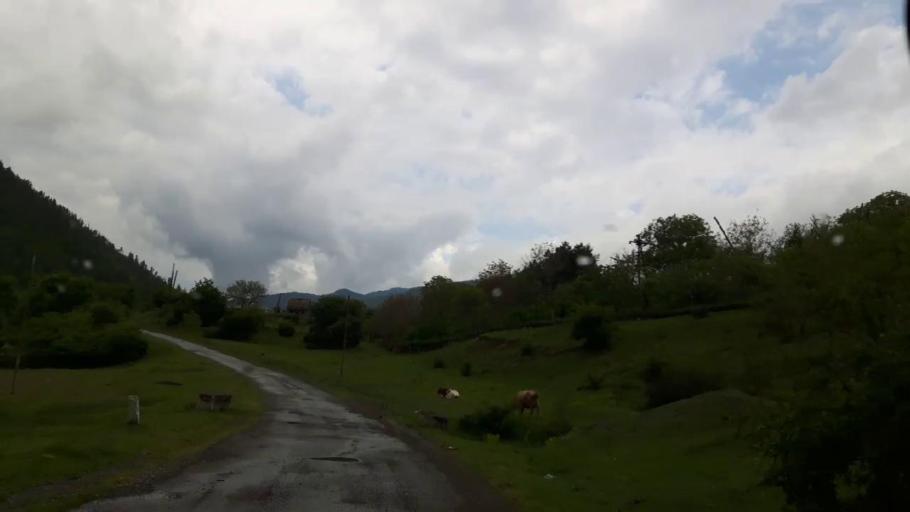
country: GE
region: Shida Kartli
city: Gori
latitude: 41.8935
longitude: 44.0241
